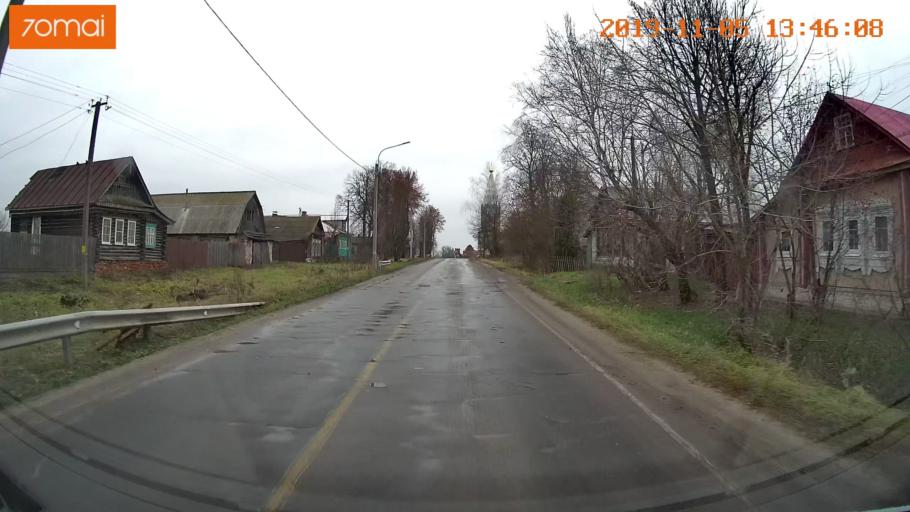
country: RU
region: Ivanovo
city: Shuya
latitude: 56.9937
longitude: 41.4101
